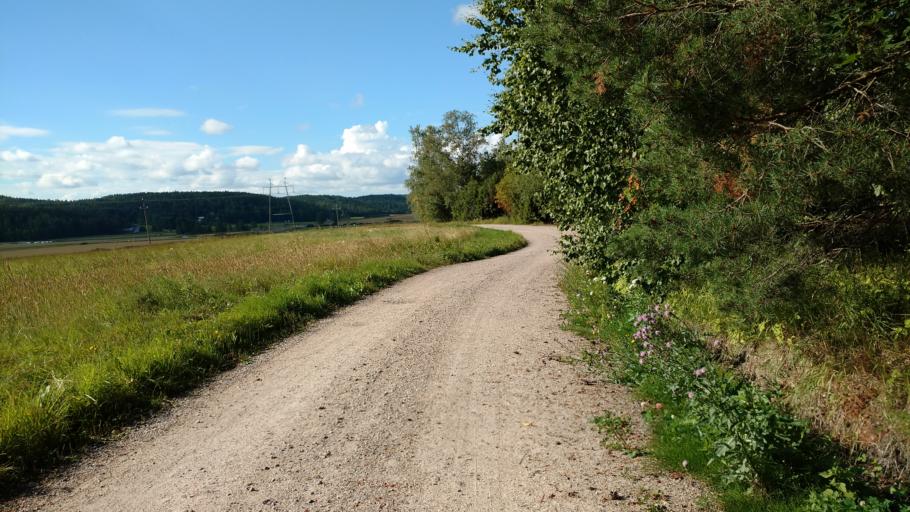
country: FI
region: Varsinais-Suomi
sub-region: Salo
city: Salo
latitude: 60.3769
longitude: 23.1680
